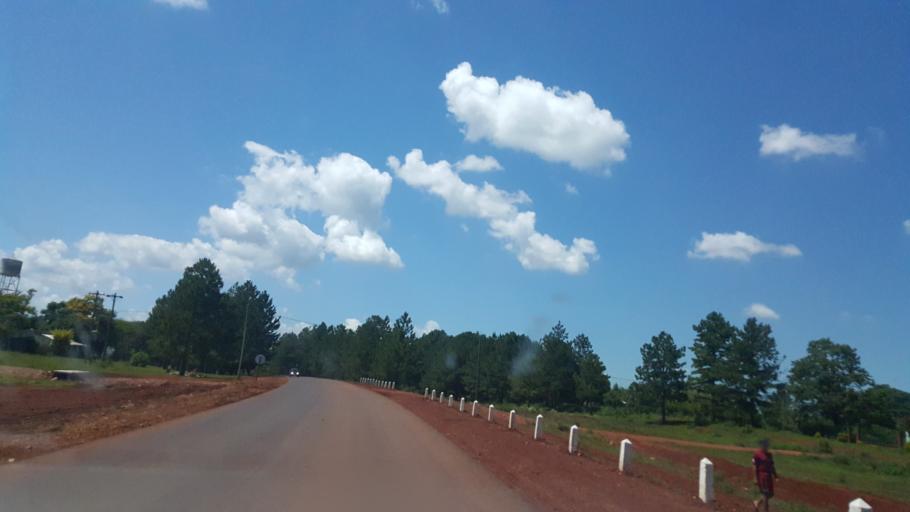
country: AR
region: Corrientes
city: Santo Tome
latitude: -28.5109
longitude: -56.0599
